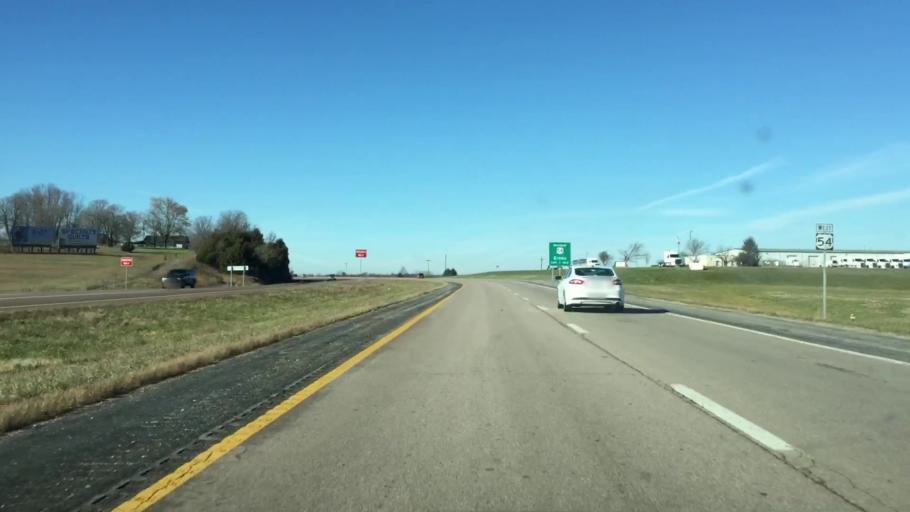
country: US
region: Missouri
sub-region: Miller County
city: Eldon
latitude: 38.3695
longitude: -92.5231
